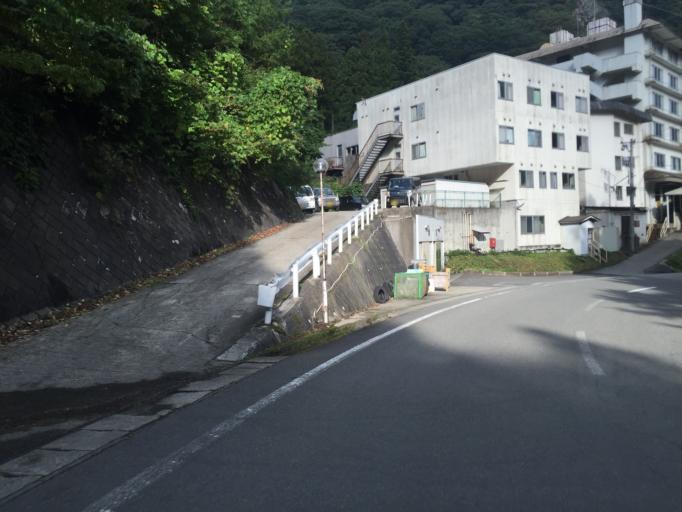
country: JP
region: Fukushima
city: Inawashiro
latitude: 37.4670
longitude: 139.9634
